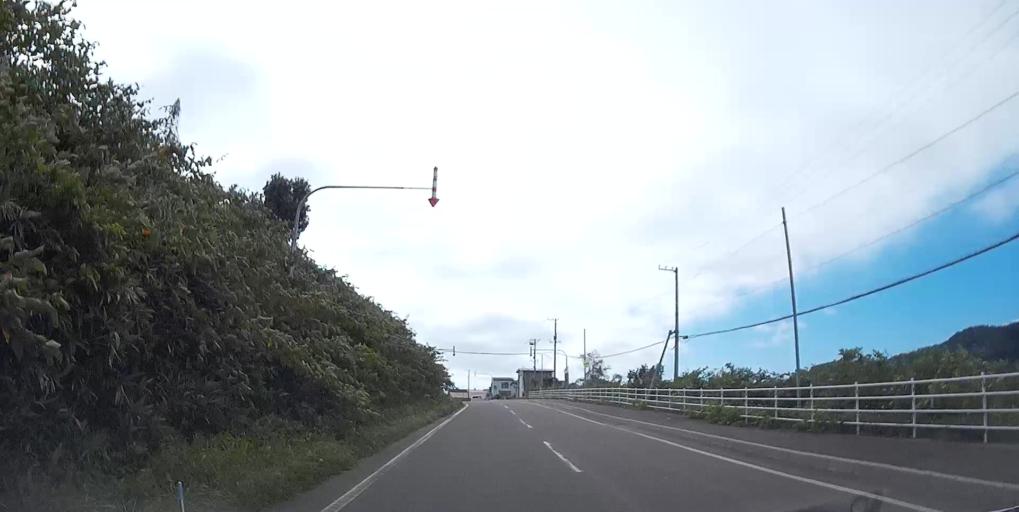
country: JP
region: Hokkaido
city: Kamiiso
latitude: 41.9714
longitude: 140.1461
